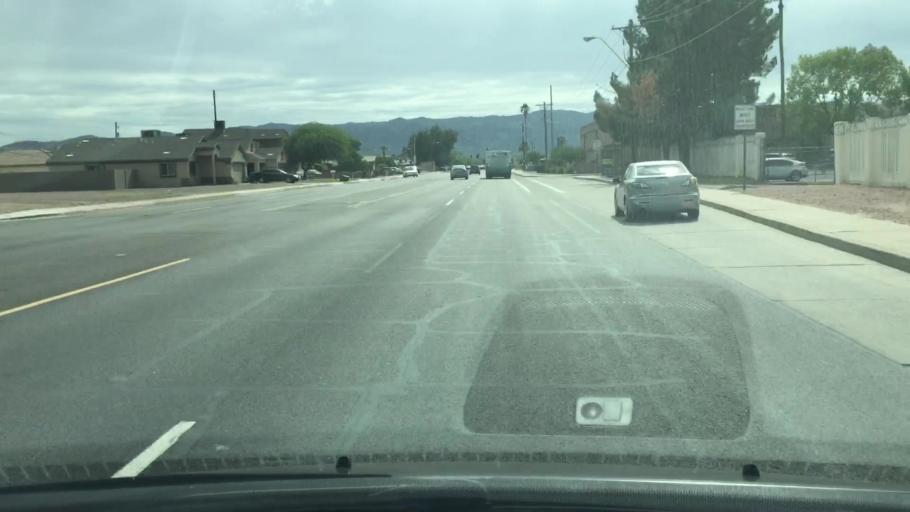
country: US
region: Arizona
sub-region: Maricopa County
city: Phoenix
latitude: 33.4107
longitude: -112.0298
